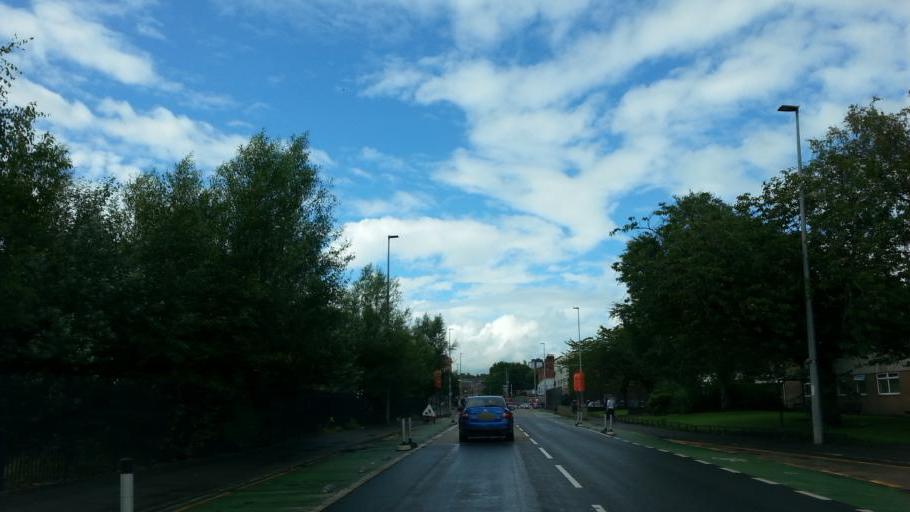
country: GB
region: England
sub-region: Manchester
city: Cheetham Hill
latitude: 53.4937
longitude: -2.2594
